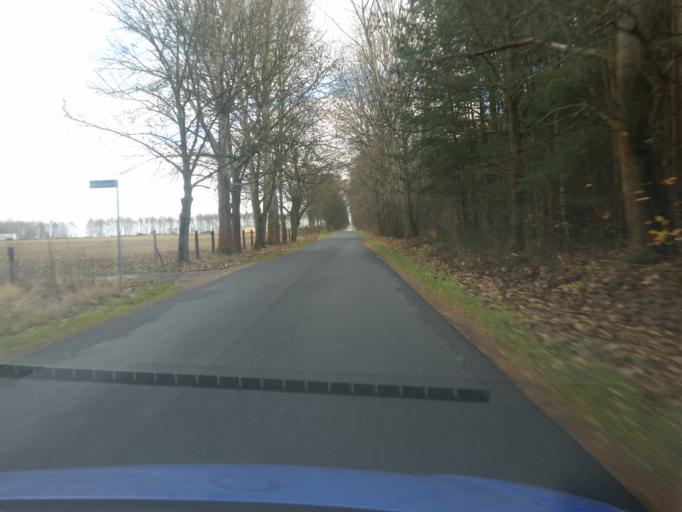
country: PL
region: Silesian Voivodeship
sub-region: Powiat czestochowski
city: Borowno
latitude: 50.9659
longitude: 19.3044
